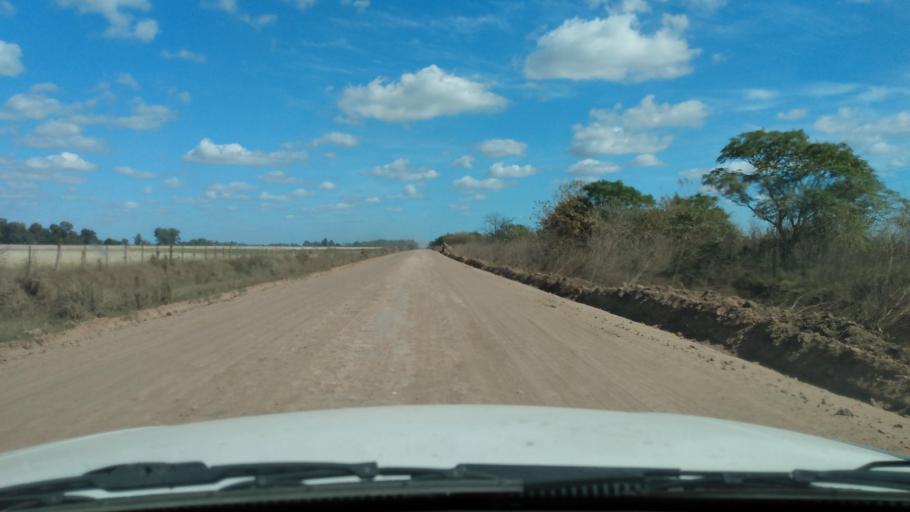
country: AR
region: Buenos Aires
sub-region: Partido de Navarro
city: Navarro
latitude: -35.0267
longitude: -59.4423
